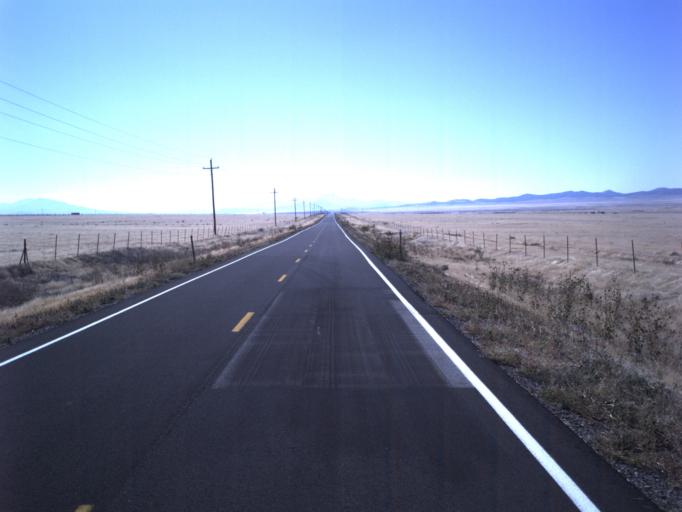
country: US
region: Utah
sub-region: Tooele County
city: Grantsville
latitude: 40.4123
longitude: -112.7485
